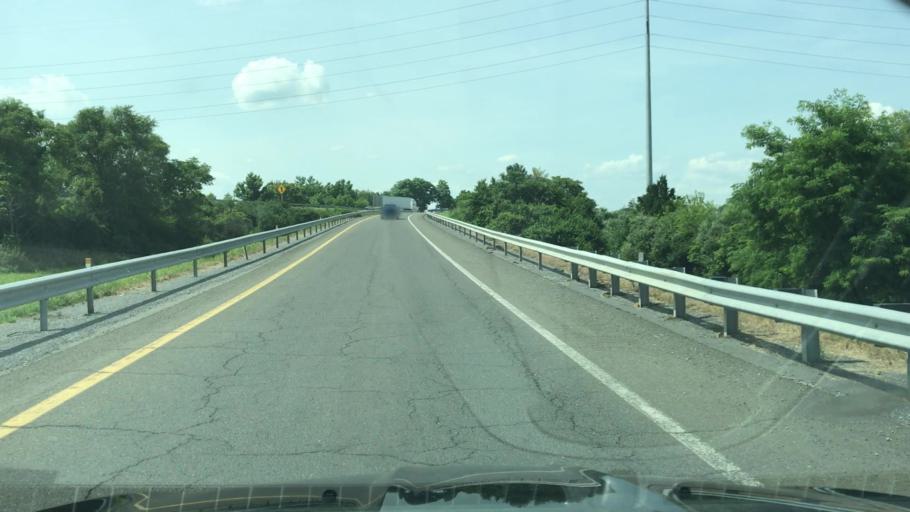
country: US
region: Virginia
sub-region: City of Winchester
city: Winchester
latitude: 39.2186
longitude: -78.1367
